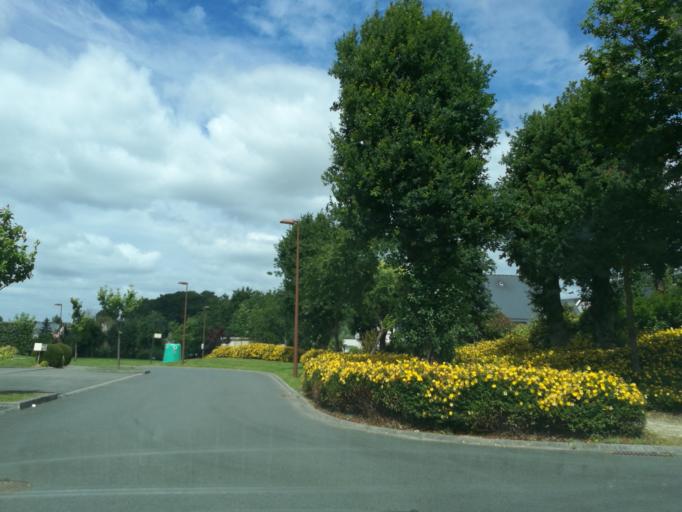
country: FR
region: Brittany
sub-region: Departement d'Ille-et-Vilaine
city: Bedee
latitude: 48.1752
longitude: -1.9424
